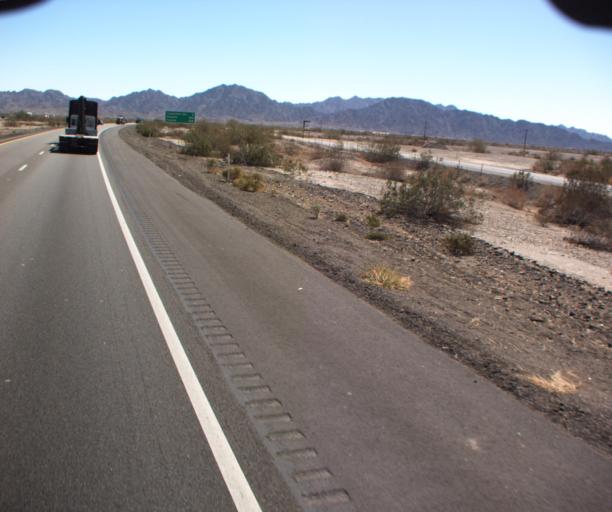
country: US
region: Arizona
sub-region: Yuma County
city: Fortuna Foothills
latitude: 32.6666
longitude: -114.3950
